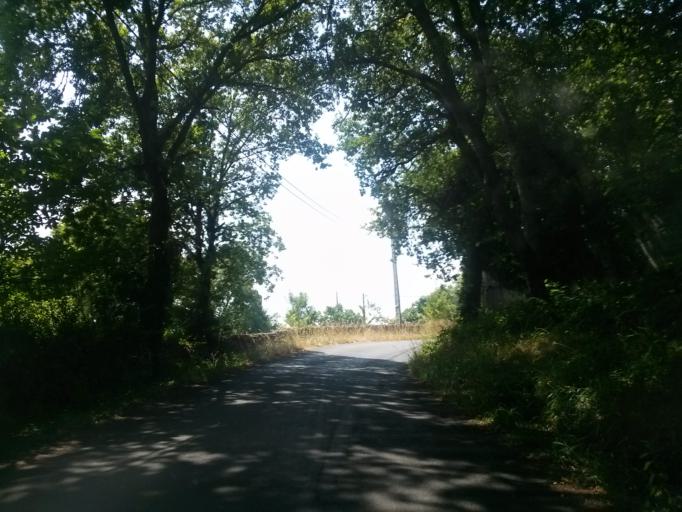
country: ES
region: Galicia
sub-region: Provincia de Lugo
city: Lugo
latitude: 43.0360
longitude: -7.5916
